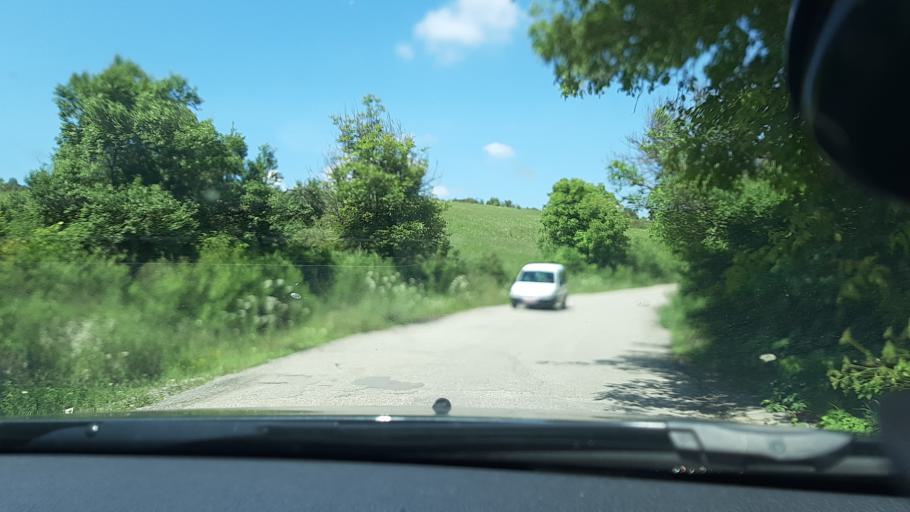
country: RO
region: Hunedoara
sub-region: Comuna Teliucu Inferior
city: Teliucu Inferior
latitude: 45.6834
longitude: 22.8719
